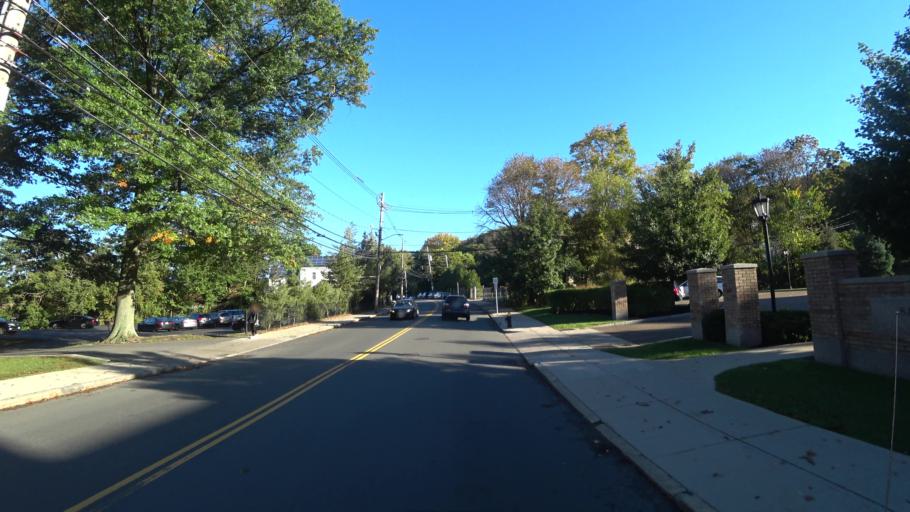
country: US
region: Massachusetts
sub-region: Middlesex County
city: Watertown
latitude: 42.3442
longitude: -71.1578
